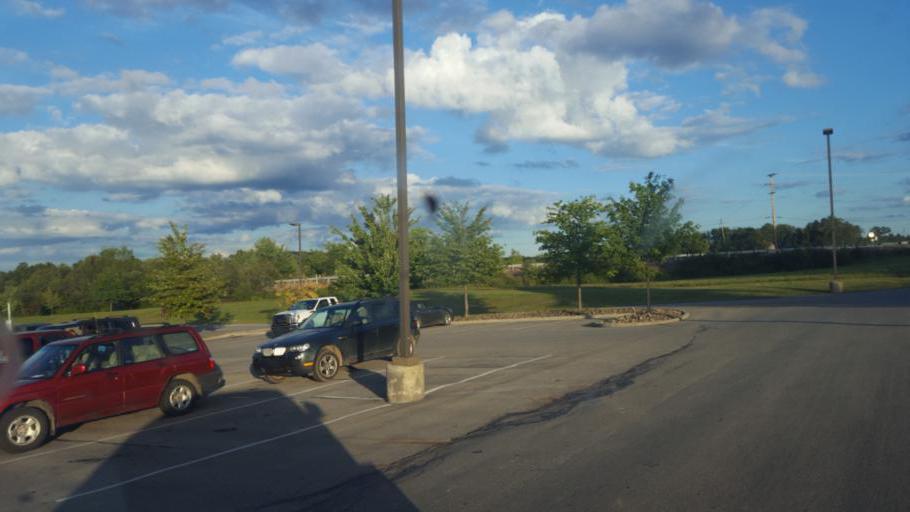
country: US
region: Pennsylvania
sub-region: Clarion County
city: Knox
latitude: 41.2152
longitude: -79.5396
